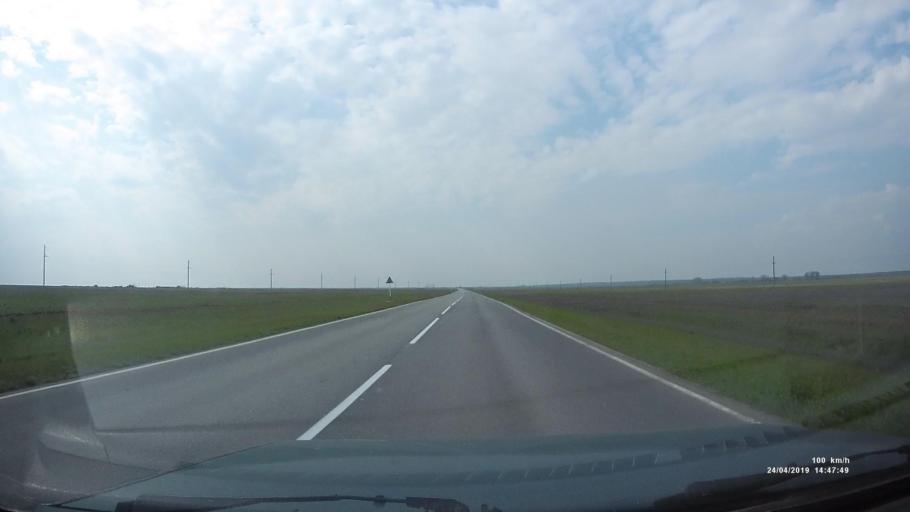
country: RU
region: Rostov
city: Remontnoye
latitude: 46.4949
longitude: 43.7669
